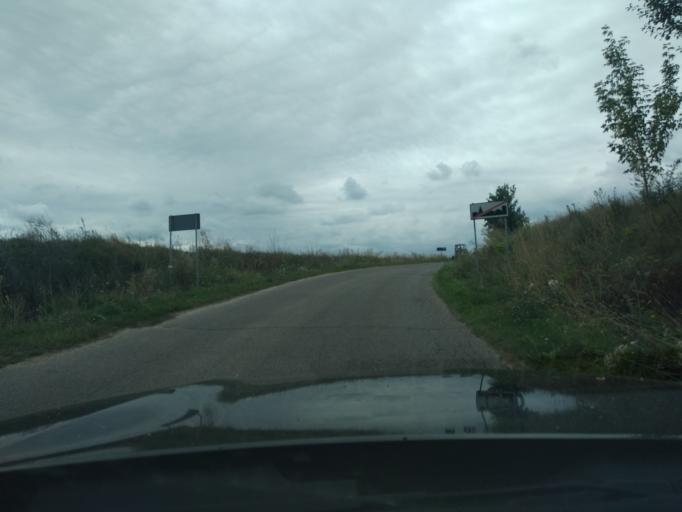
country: PL
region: Masovian Voivodeship
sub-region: Powiat pultuski
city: Obryte
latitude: 52.7545
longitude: 21.2170
